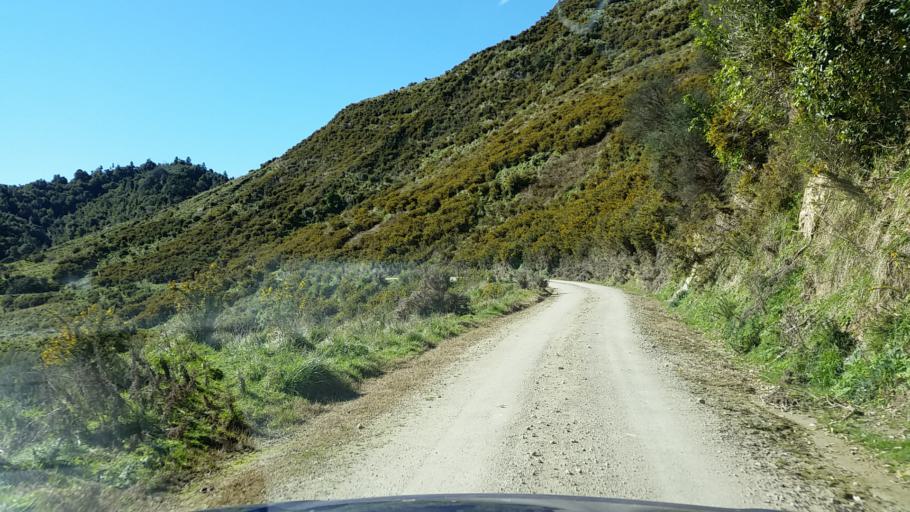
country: NZ
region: Manawatu-Wanganui
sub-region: Wanganui District
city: Wanganui
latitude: -39.6656
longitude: 174.8744
